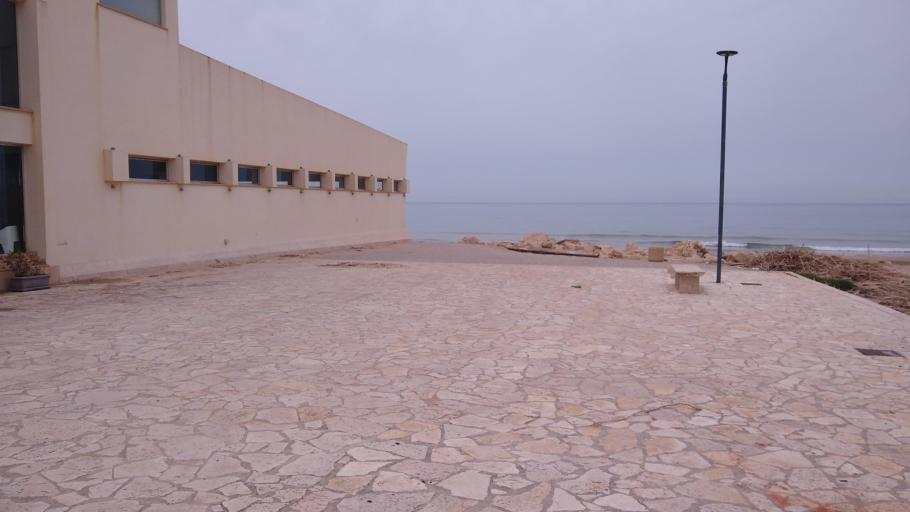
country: IT
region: Sicily
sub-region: Trapani
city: Alcamo
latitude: 38.0281
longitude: 12.9344
